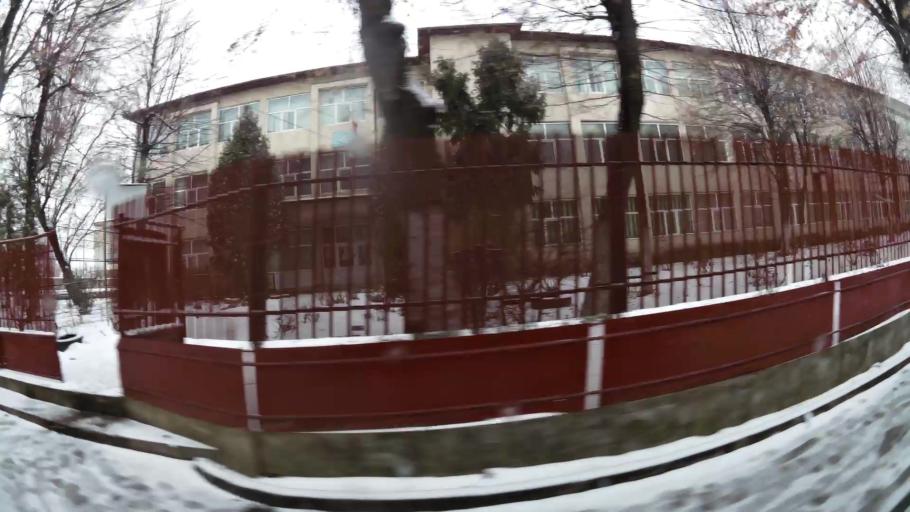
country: RO
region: Dambovita
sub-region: Municipiul Targoviste
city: Targoviste
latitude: 44.9254
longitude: 25.4428
